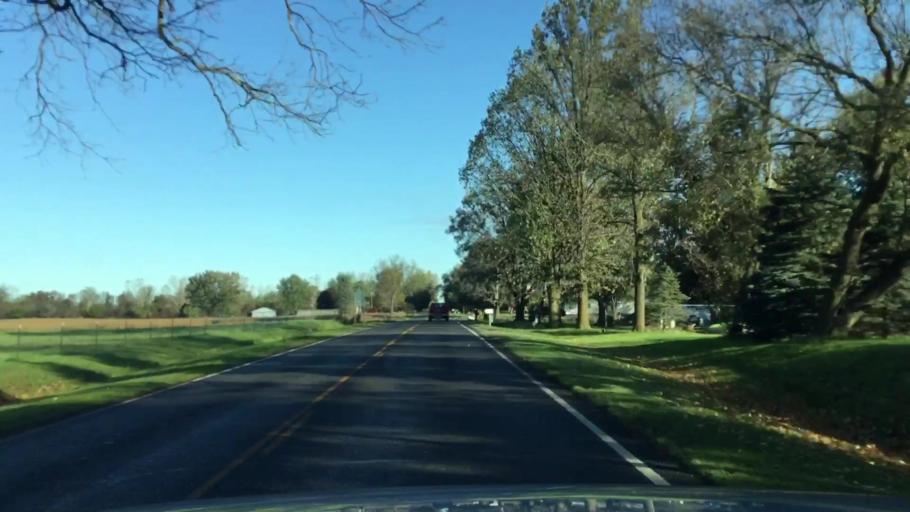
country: US
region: Michigan
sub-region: Shiawassee County
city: Durand
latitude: 42.8392
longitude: -83.9452
